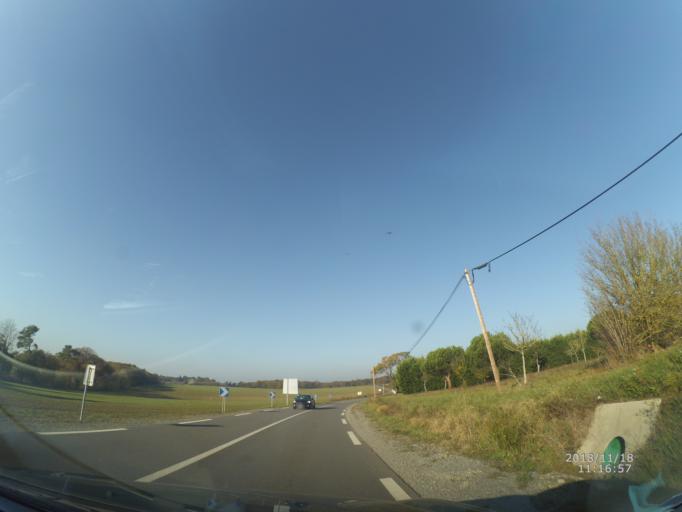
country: FR
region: Pays de la Loire
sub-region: Departement de la Loire-Atlantique
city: Saint-Pere-en-Retz
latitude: 47.2162
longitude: -2.0567
